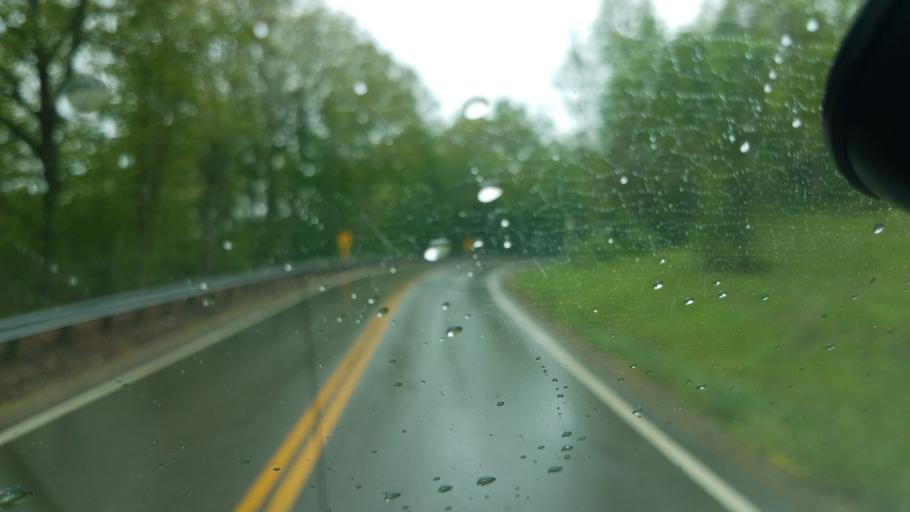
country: US
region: Ohio
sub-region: Muskingum County
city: Dresden
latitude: 40.1708
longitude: -82.0284
